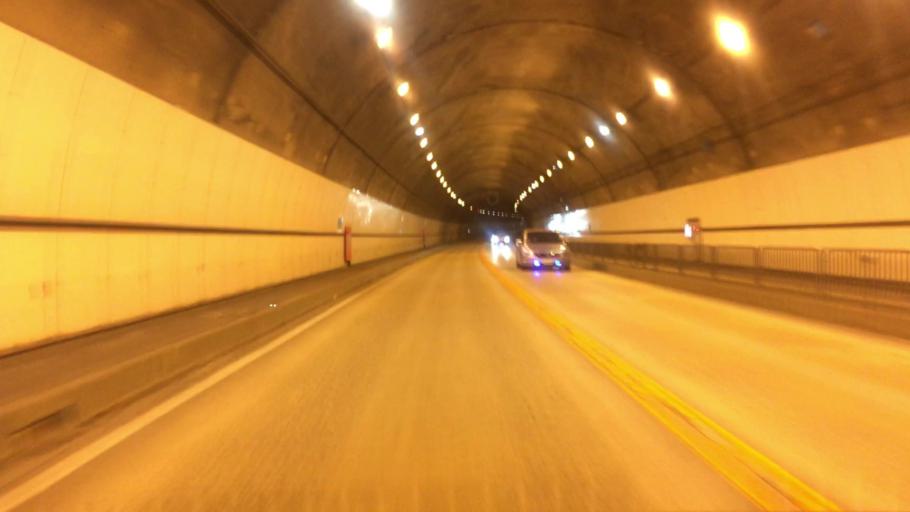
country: JP
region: Hyogo
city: Toyooka
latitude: 35.3859
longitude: 134.7771
